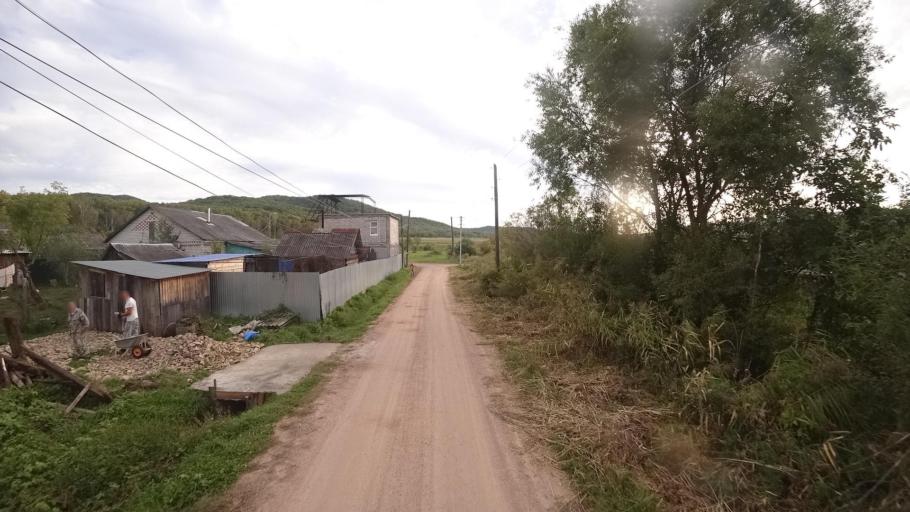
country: RU
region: Primorskiy
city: Yakovlevka
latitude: 44.4133
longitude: 133.4492
